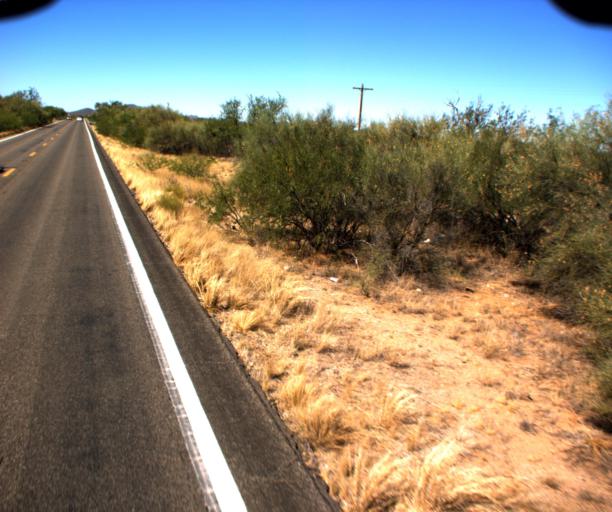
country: US
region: Arizona
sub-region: Pima County
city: Sells
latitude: 31.9560
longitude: -111.7564
